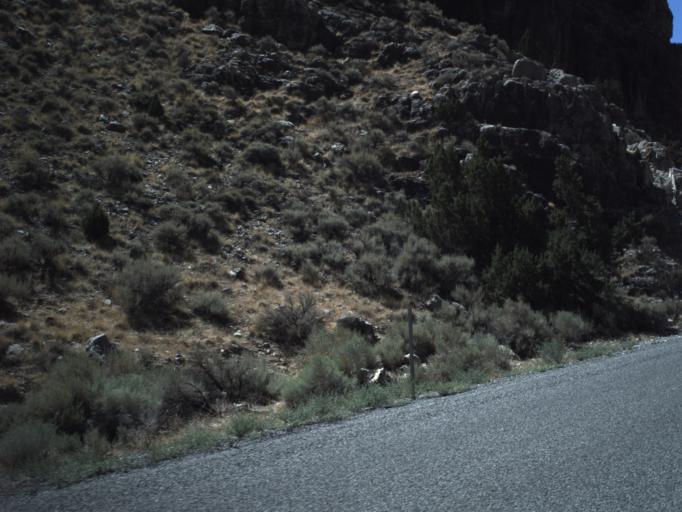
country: US
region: Utah
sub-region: Beaver County
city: Milford
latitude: 39.0864
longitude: -113.5685
